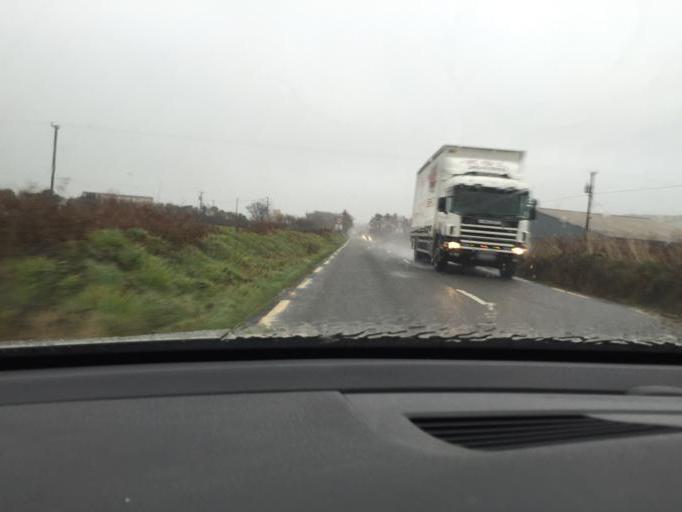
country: IE
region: Munster
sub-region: Ciarrai
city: Dingle
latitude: 52.1407
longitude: -10.1764
